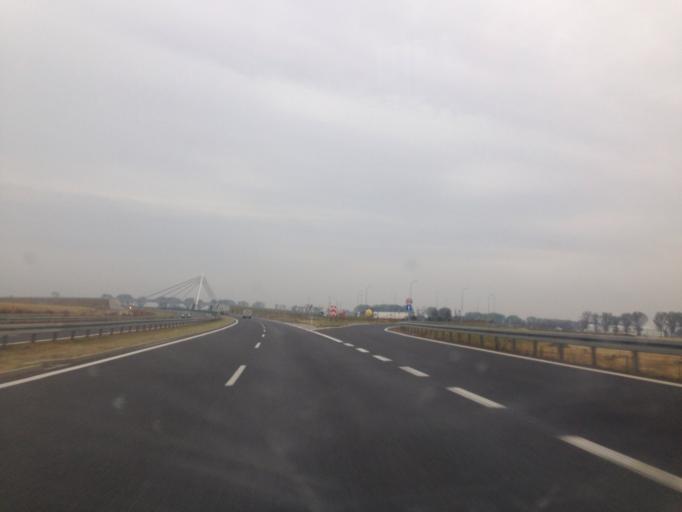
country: PL
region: Greater Poland Voivodeship
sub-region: Powiat poznanski
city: Kostrzyn
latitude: 52.3705
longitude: 17.2090
